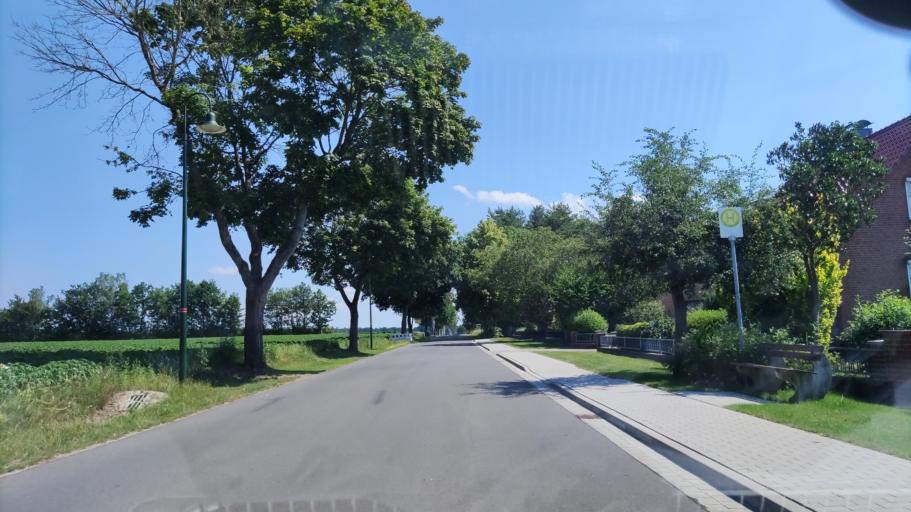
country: DE
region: Lower Saxony
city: Suderburg
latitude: 52.8795
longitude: 10.4122
